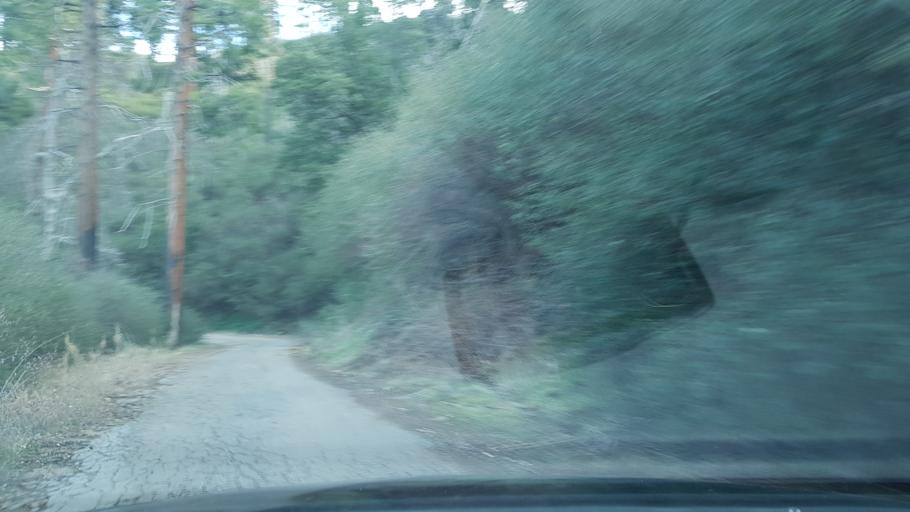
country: US
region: California
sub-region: Riverside County
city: Aguanga
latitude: 33.3362
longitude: -116.9167
